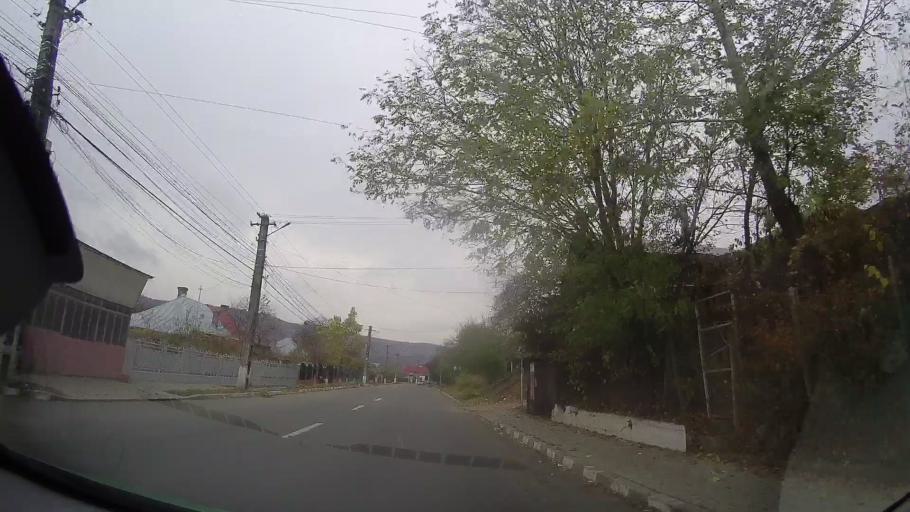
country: RO
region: Prahova
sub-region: Oras Urlati
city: Urlati
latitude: 44.9972
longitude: 26.2294
